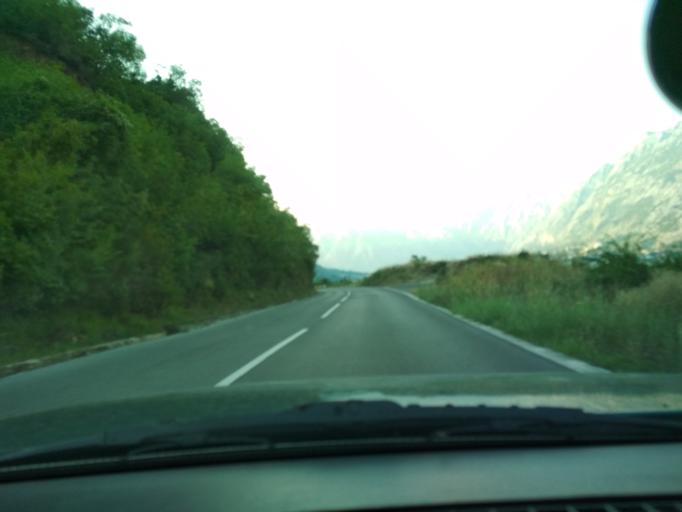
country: ME
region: Kotor
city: Kotor
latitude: 42.4099
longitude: 18.7647
